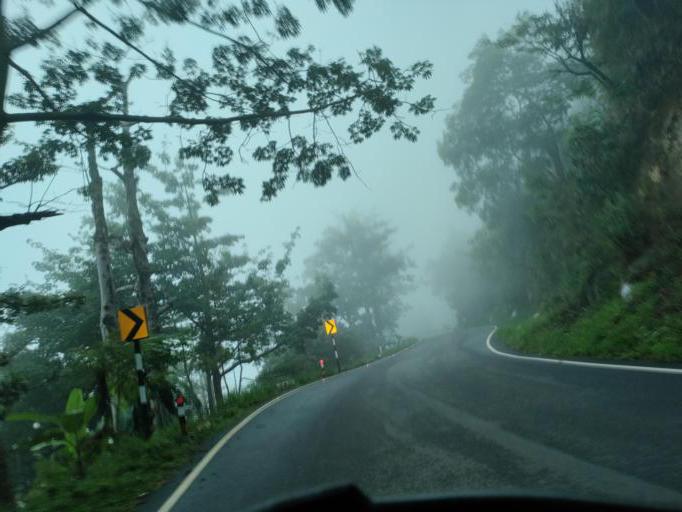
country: IN
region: Tamil Nadu
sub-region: Dindigul
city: Ayakudi
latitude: 10.3490
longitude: 77.5743
